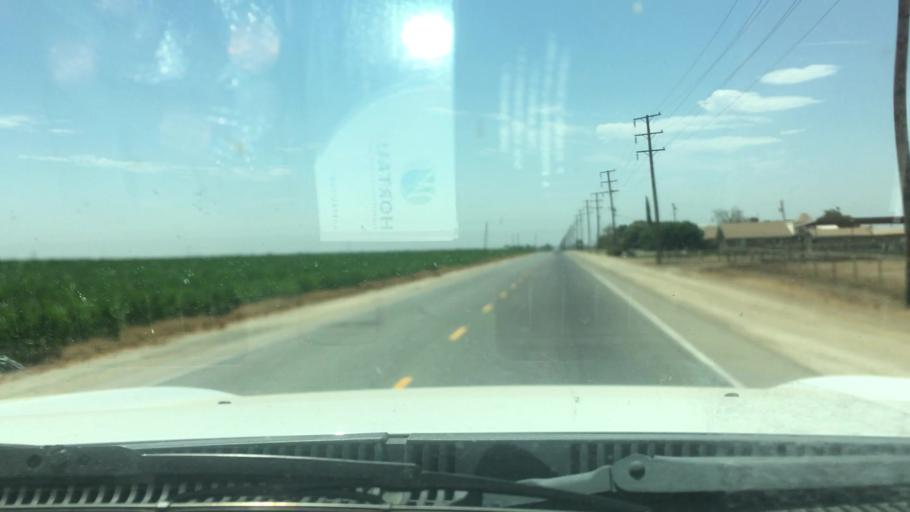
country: US
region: California
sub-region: Tulare County
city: Tipton
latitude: 36.0657
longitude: -119.2615
